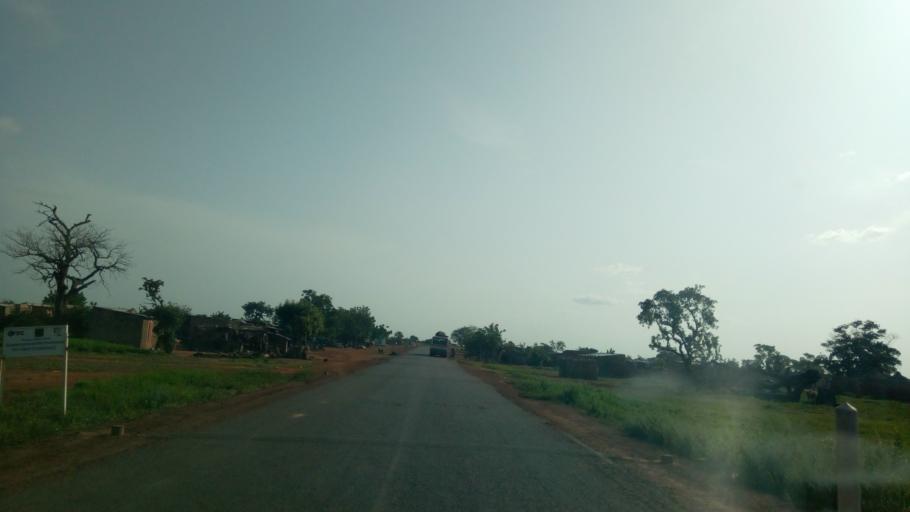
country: ML
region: Sikasso
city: Koutiala
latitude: 12.5231
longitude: -5.2541
